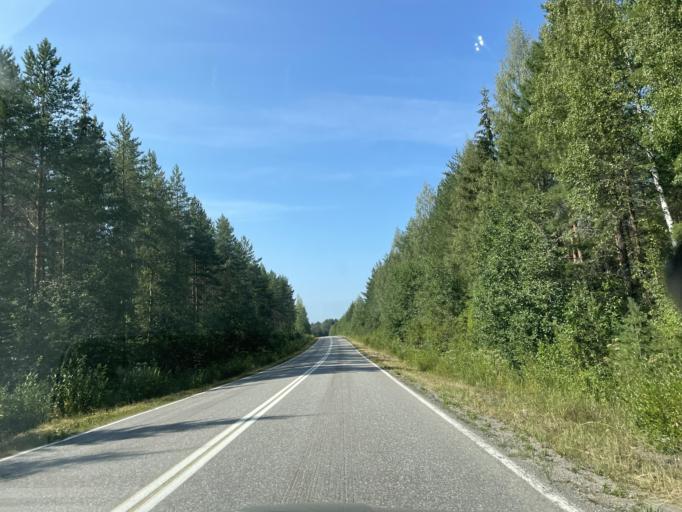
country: FI
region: Central Finland
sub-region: Saarijaervi-Viitasaari
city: Pihtipudas
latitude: 63.3654
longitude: 25.6662
